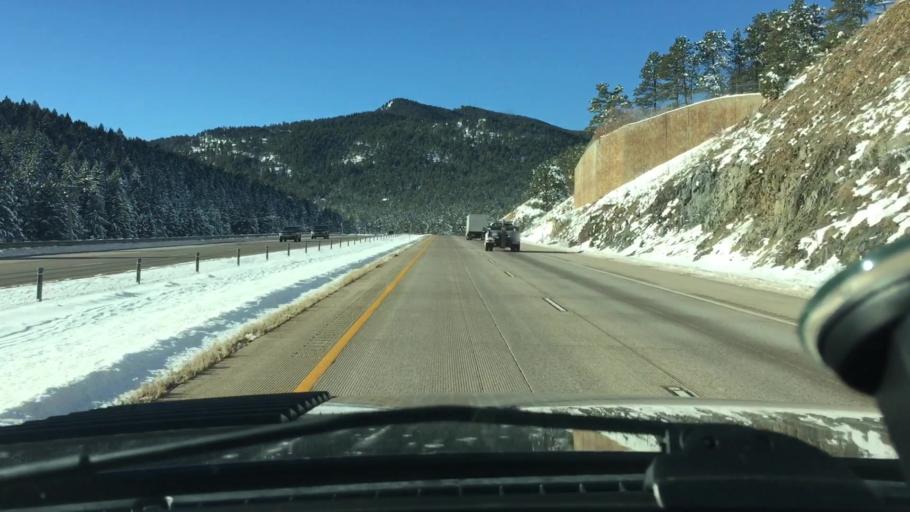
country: US
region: Colorado
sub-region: Jefferson County
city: Indian Hills
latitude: 39.5792
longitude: -105.2342
